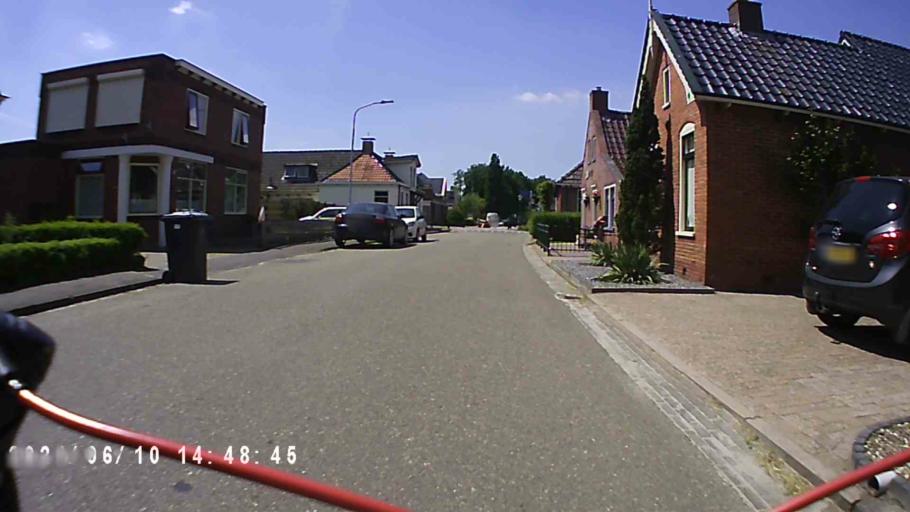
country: NL
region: Groningen
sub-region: Gemeente Grootegast
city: Grootegast
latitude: 53.2350
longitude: 6.2581
